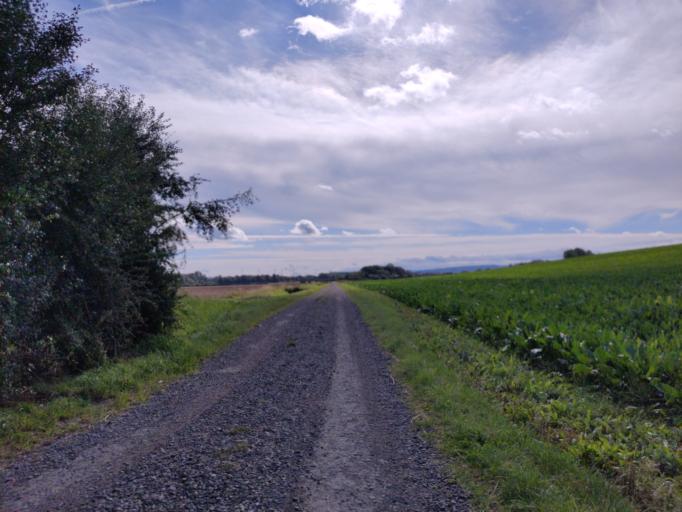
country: DE
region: Lower Saxony
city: Baddeckenstedt
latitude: 52.0771
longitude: 10.2407
